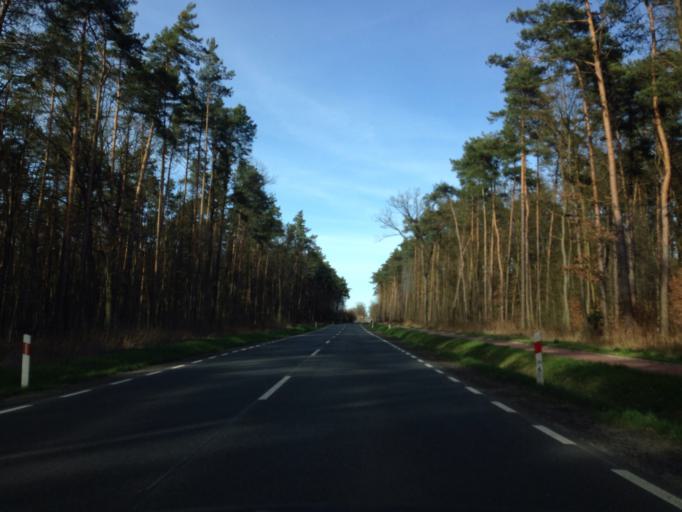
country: PL
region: Lodz Voivodeship
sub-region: Powiat poddebicki
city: Wartkowice
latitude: 51.9622
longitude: 19.0106
